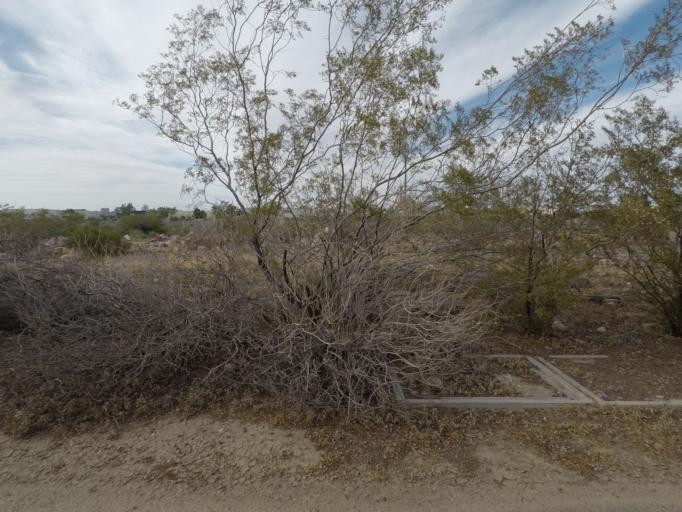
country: US
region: Arizona
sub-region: Maricopa County
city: Phoenix
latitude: 33.4197
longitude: -112.0598
